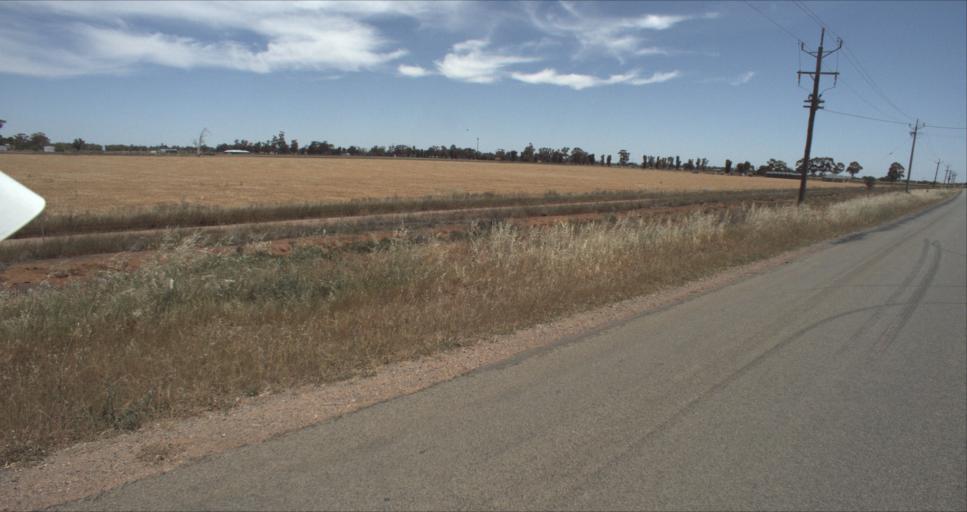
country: AU
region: New South Wales
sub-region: Leeton
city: Leeton
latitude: -34.5860
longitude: 146.4209
